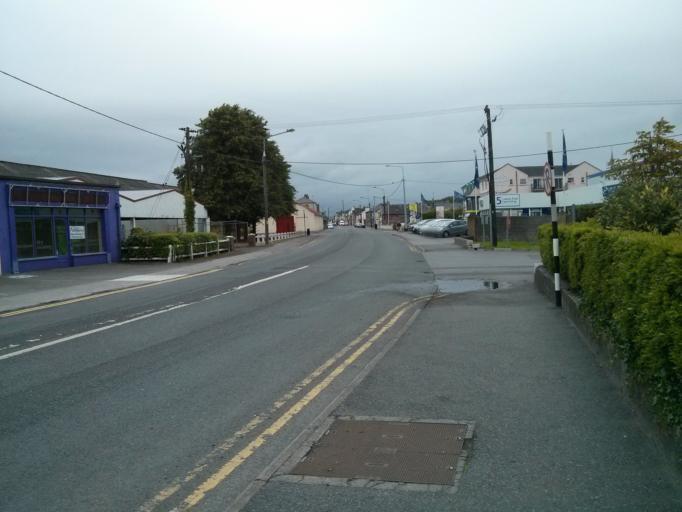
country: IE
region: Leinster
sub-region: Uibh Fhaili
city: Tullamore
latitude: 53.2733
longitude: -7.4853
